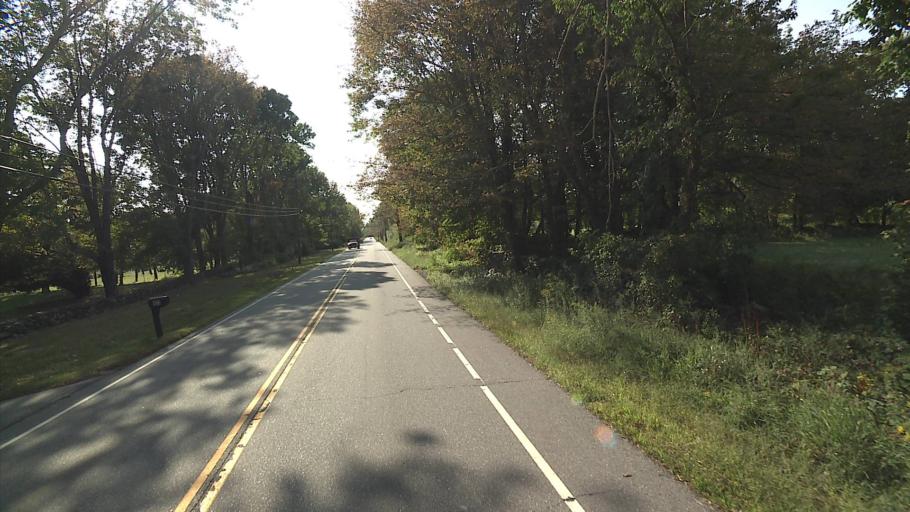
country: US
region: Connecticut
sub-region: Tolland County
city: South Coventry
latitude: 41.6905
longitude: -72.2890
